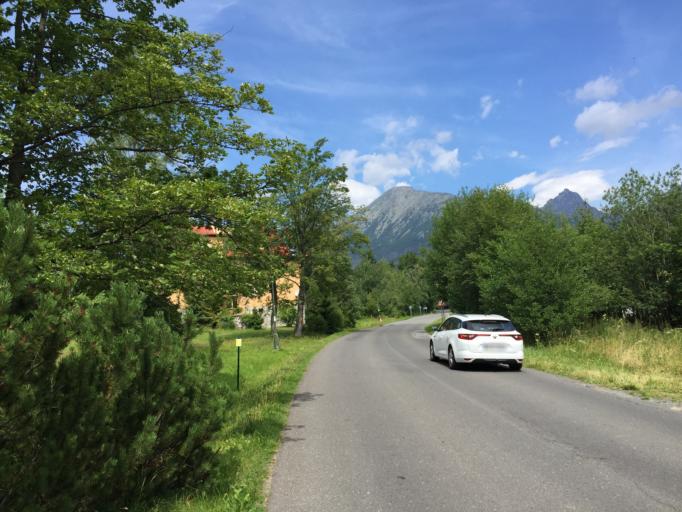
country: SK
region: Presovsky
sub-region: Okres Poprad
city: Vysoke Tatry
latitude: 49.1282
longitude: 20.2487
